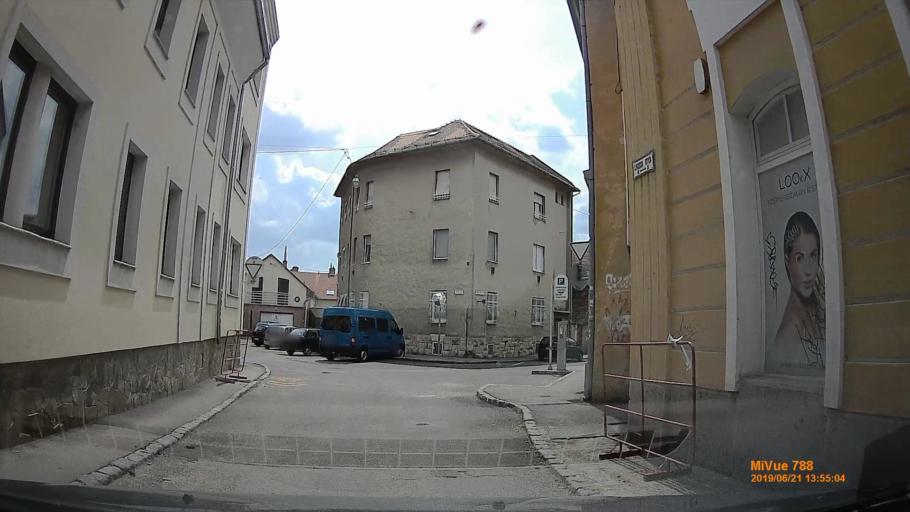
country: HU
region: Baranya
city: Pecs
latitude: 46.0759
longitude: 18.2349
